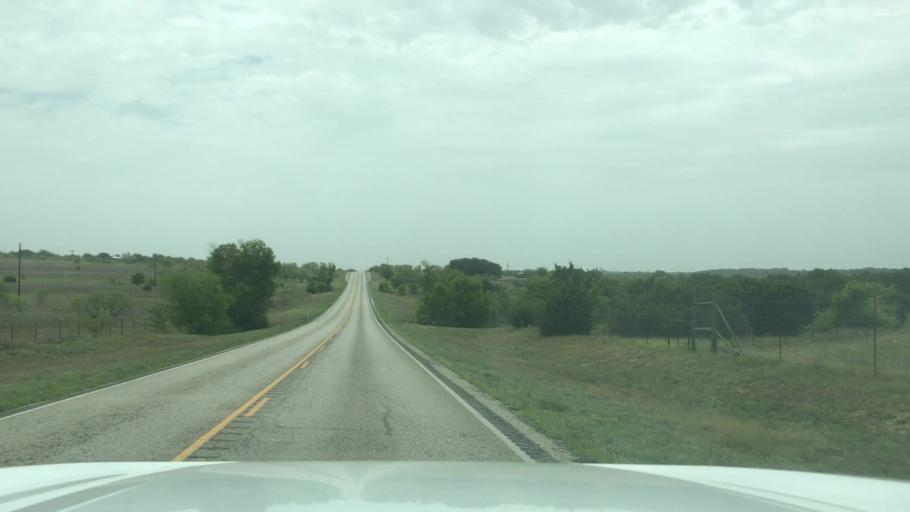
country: US
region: Texas
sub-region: Hamilton County
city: Hico
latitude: 32.0526
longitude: -98.1696
